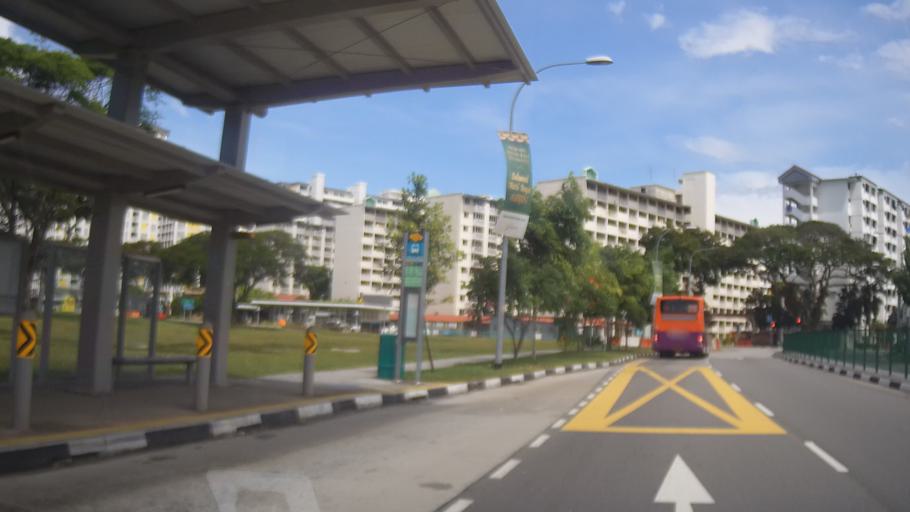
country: SG
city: Singapore
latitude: 1.3271
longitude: 103.8891
